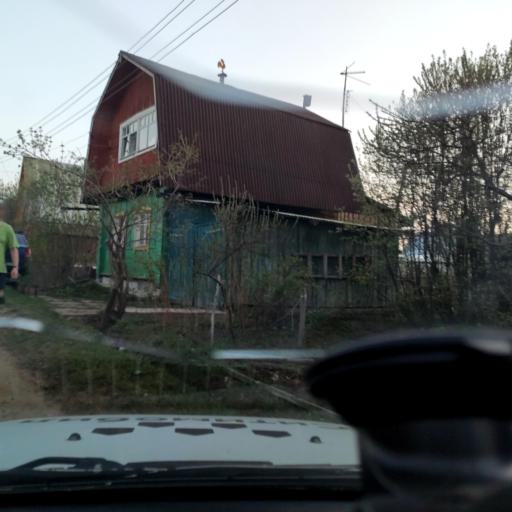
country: RU
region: Perm
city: Yug
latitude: 57.5864
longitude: 56.1995
